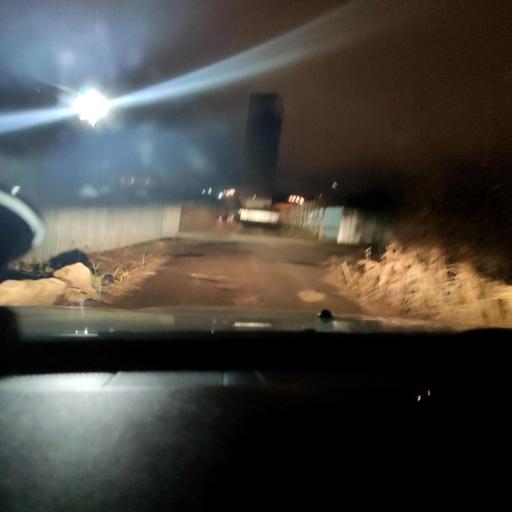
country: RU
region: Samara
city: Samara
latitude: 53.2275
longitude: 50.2192
